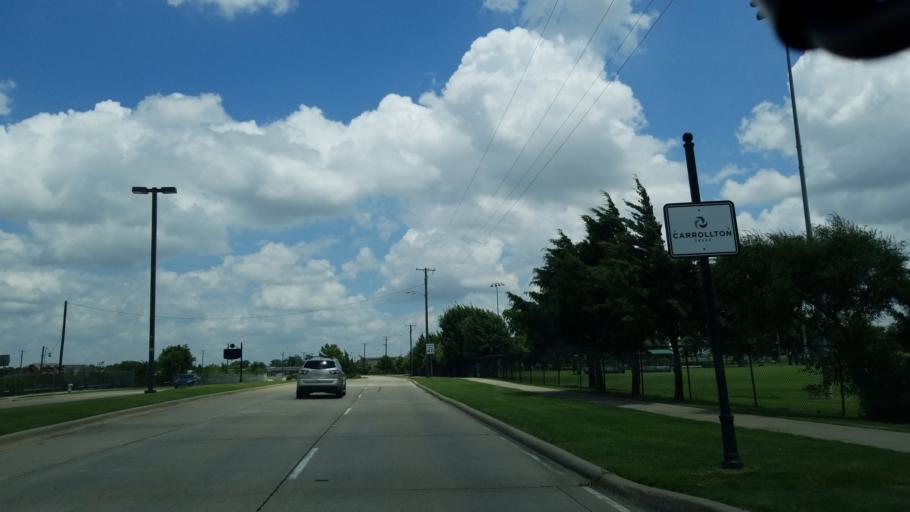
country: US
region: Texas
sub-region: Dallas County
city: Carrollton
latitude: 32.9658
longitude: -96.9399
